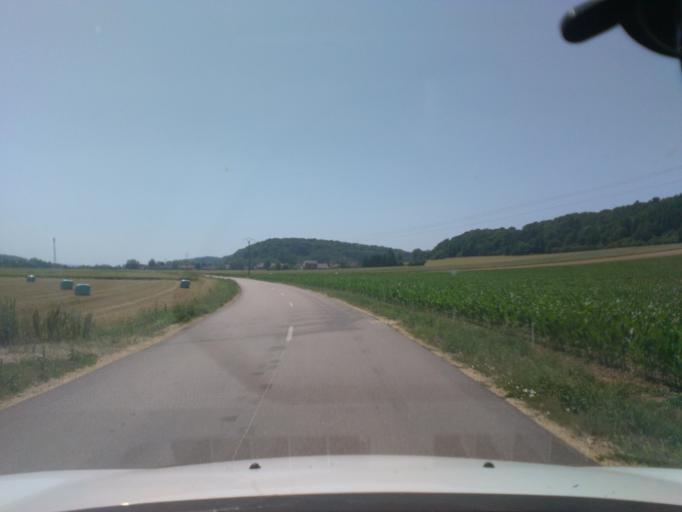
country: FR
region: Lorraine
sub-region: Departement des Vosges
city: Liffol-le-Grand
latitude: 48.3737
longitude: 5.6145
